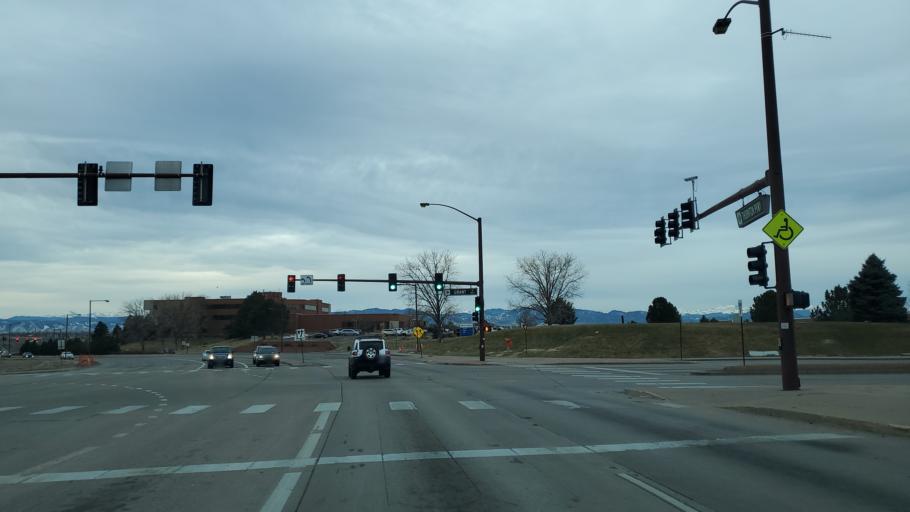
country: US
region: Colorado
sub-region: Adams County
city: Thornton
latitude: 39.8706
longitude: -104.9812
